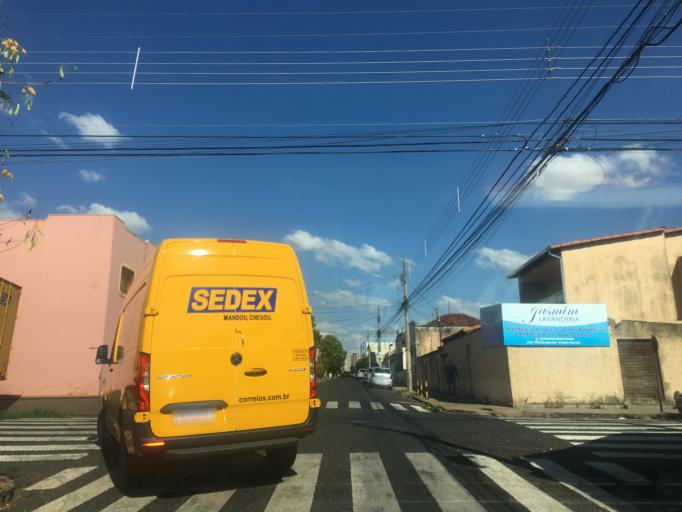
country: BR
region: Minas Gerais
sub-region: Uberlandia
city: Uberlandia
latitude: -18.9076
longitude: -48.2819
